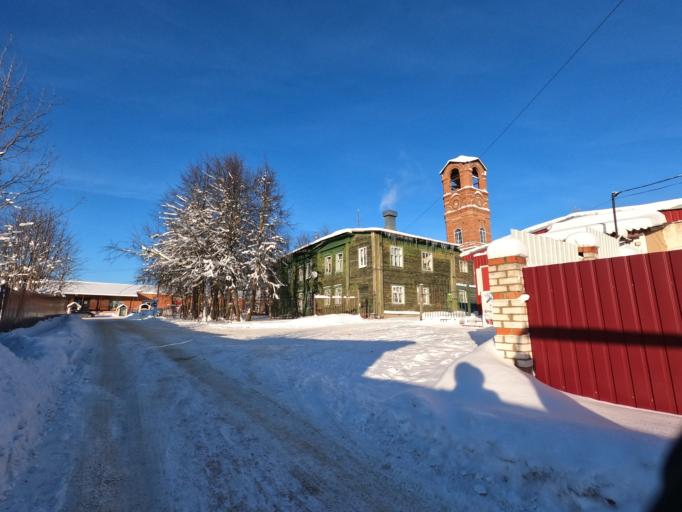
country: RU
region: Moskovskaya
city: Taldom
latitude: 56.7297
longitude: 37.5268
